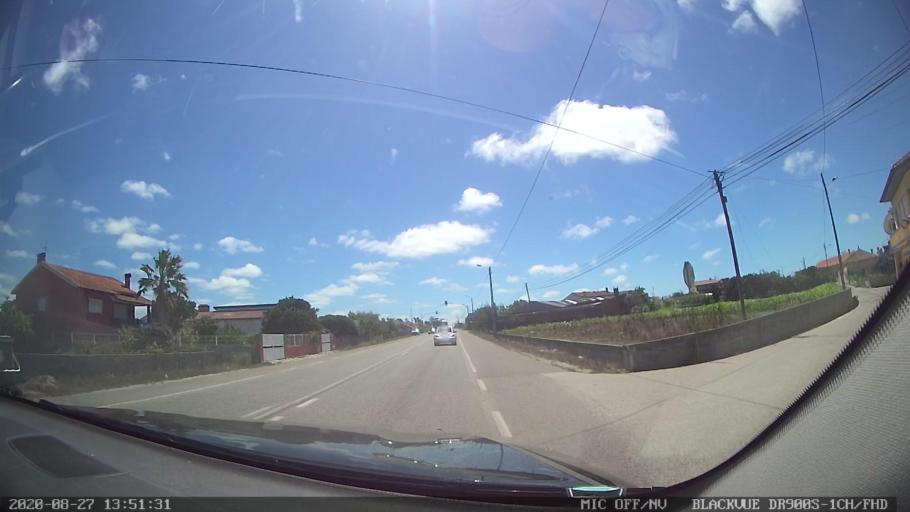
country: PT
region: Coimbra
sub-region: Mira
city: Mira
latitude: 40.3470
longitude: -8.7490
